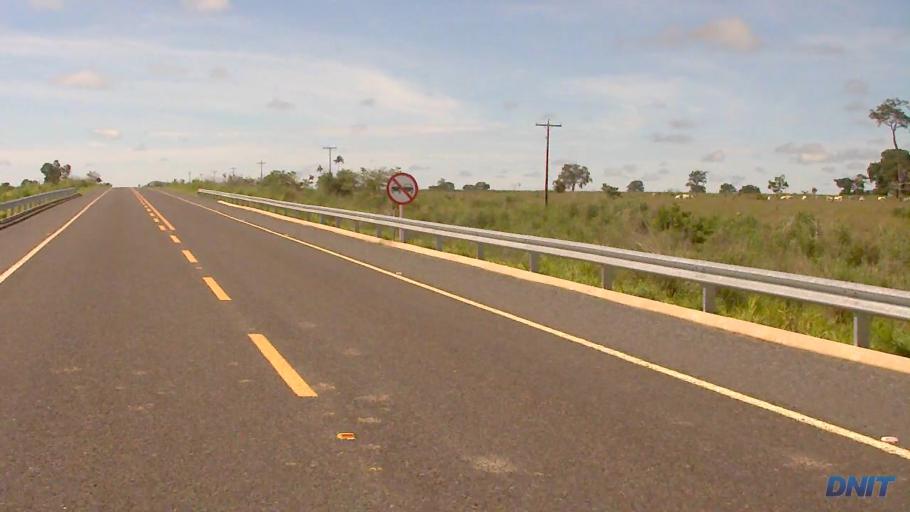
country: BR
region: Goias
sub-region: Sao Miguel Do Araguaia
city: Sao Miguel do Araguaia
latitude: -13.3469
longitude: -50.1505
